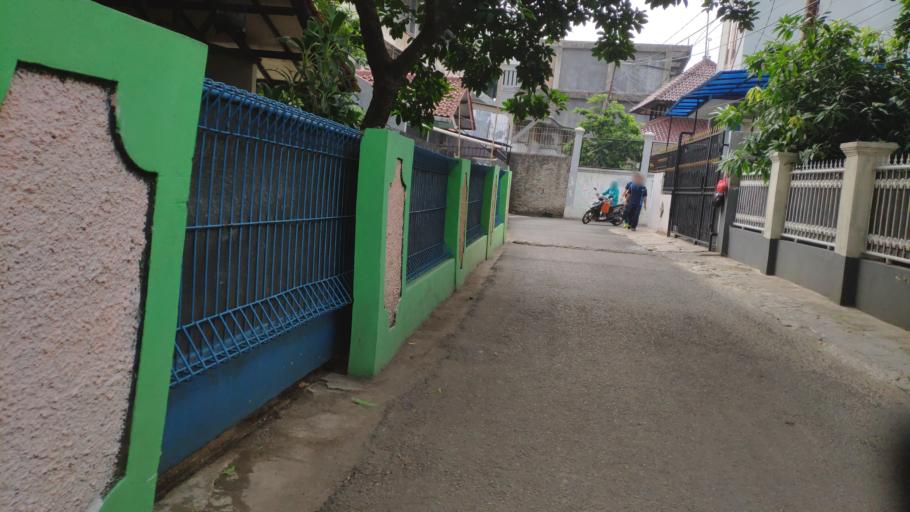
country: ID
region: West Java
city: Depok
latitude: -6.3481
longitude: 106.8109
